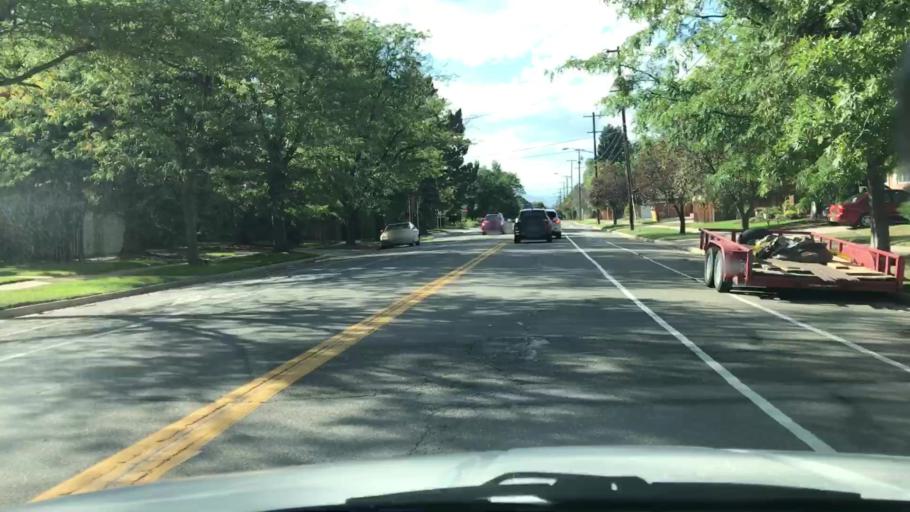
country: US
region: Colorado
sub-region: Arapahoe County
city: Cherry Hills Village
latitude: 39.6464
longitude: -104.9230
